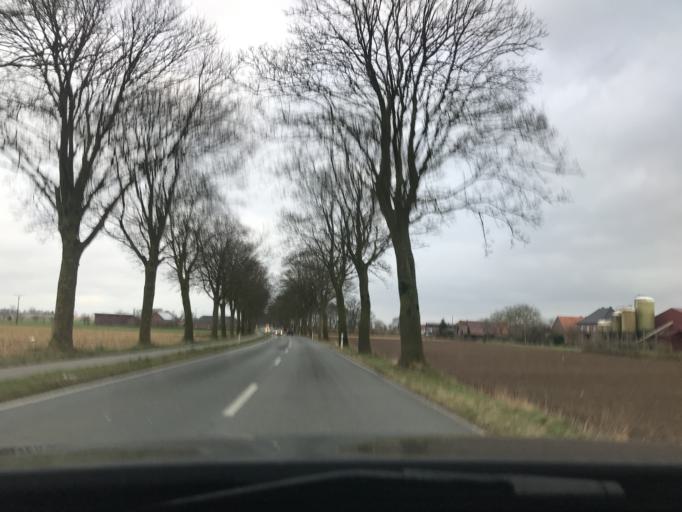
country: DE
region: North Rhine-Westphalia
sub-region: Regierungsbezirk Dusseldorf
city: Goch
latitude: 51.7333
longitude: 6.2034
